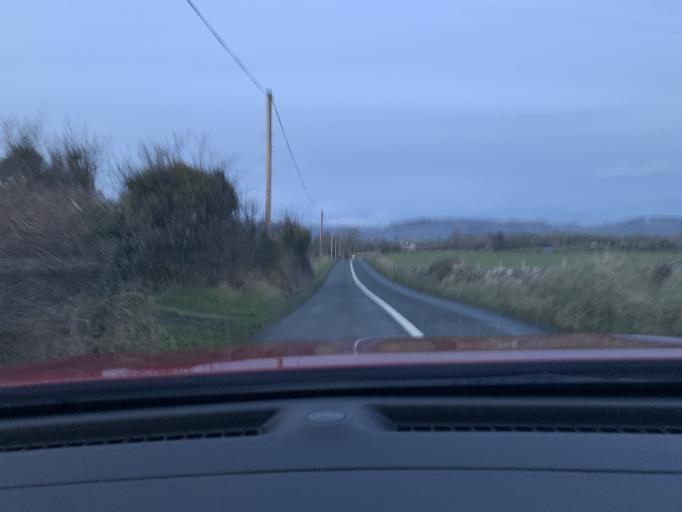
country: IE
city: Ballisodare
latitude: 54.2521
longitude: -8.5165
